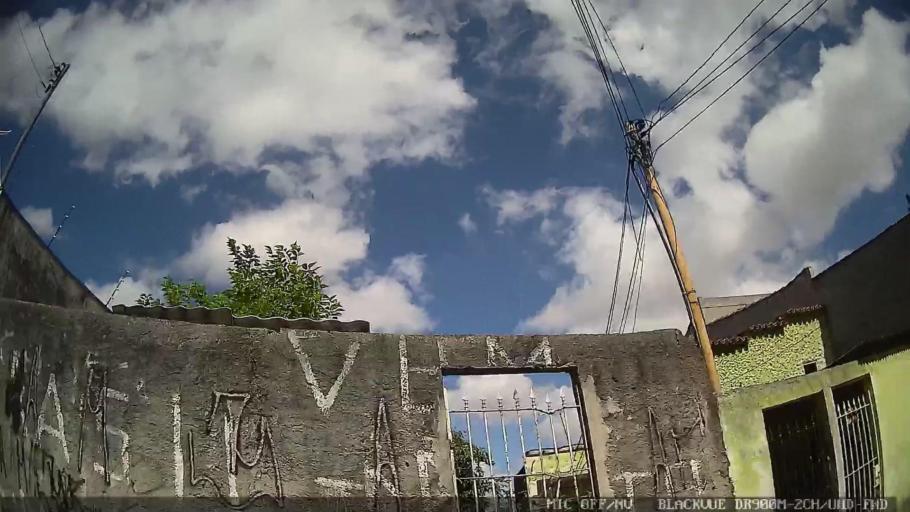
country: BR
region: Sao Paulo
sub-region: Sao Caetano Do Sul
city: Sao Caetano do Sul
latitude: -23.6257
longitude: -46.5880
